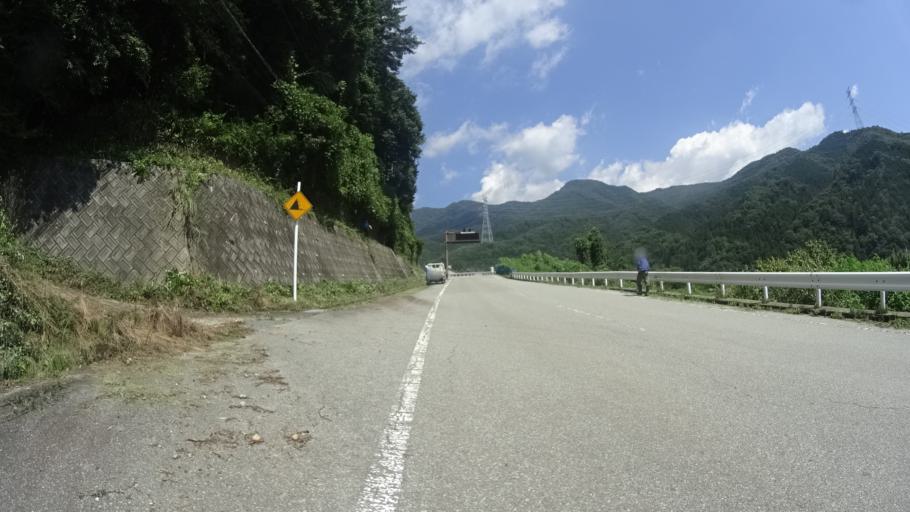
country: JP
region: Yamanashi
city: Enzan
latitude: 35.7731
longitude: 138.6971
